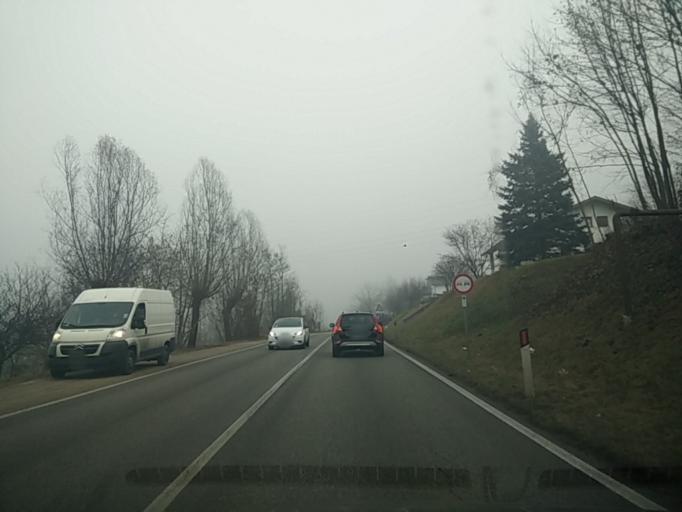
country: IT
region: Veneto
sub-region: Provincia di Belluno
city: Villabruna-Umin
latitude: 46.0265
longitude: 11.9318
